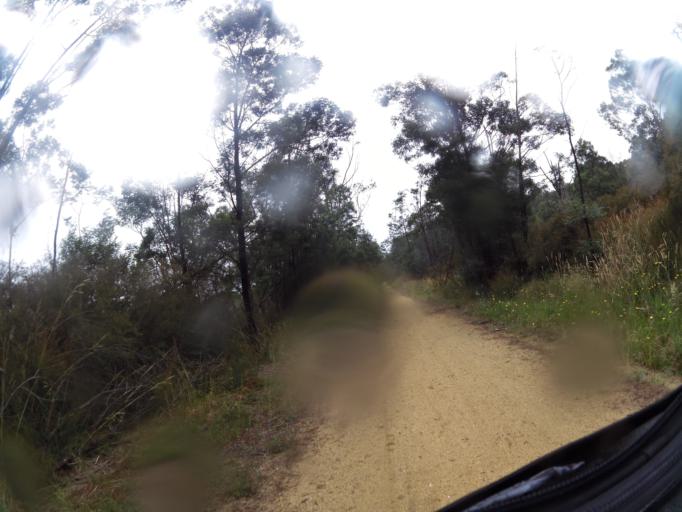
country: AU
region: Victoria
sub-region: East Gippsland
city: Lakes Entrance
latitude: -37.7501
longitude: 147.8118
